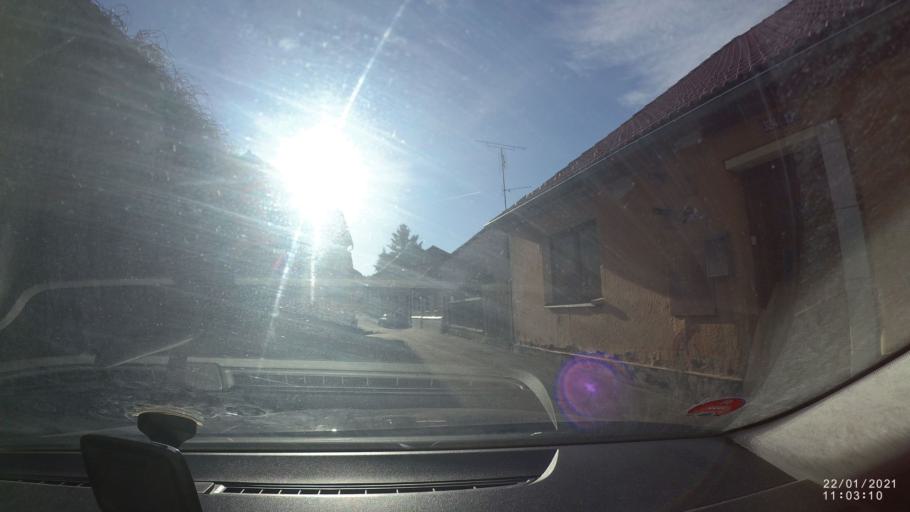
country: CZ
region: Central Bohemia
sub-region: Okres Beroun
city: Horovice
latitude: 49.8364
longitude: 13.9002
